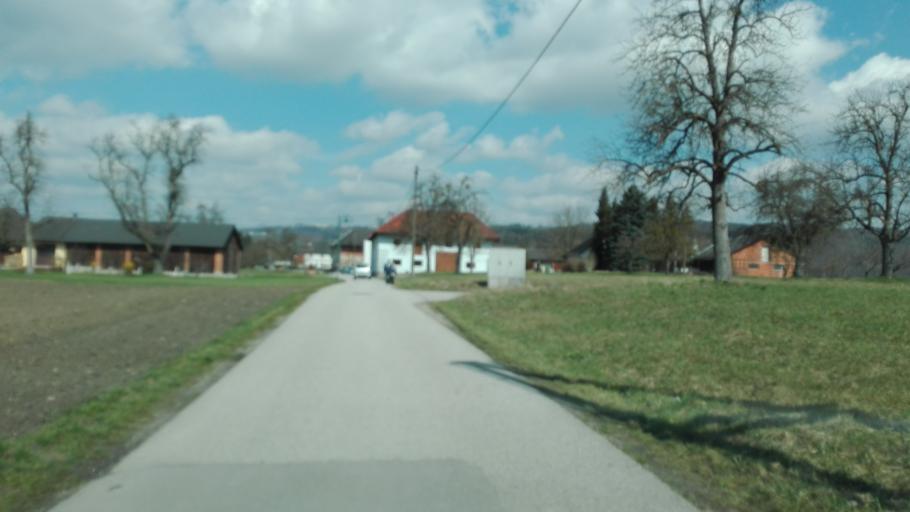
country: AT
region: Upper Austria
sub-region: Politischer Bezirk Urfahr-Umgebung
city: Feldkirchen an der Donau
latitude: 48.3541
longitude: 14.0281
